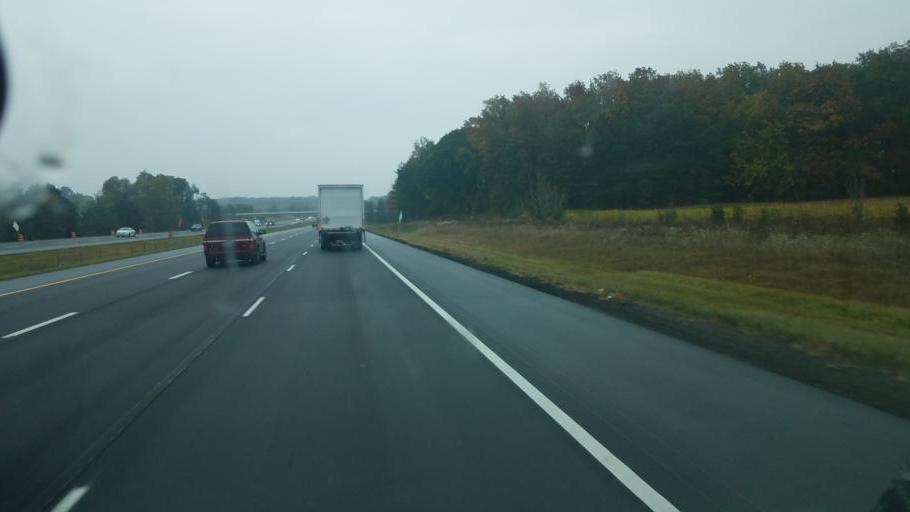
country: US
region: Ohio
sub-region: Ashland County
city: Ashland
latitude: 40.8276
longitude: -82.3215
